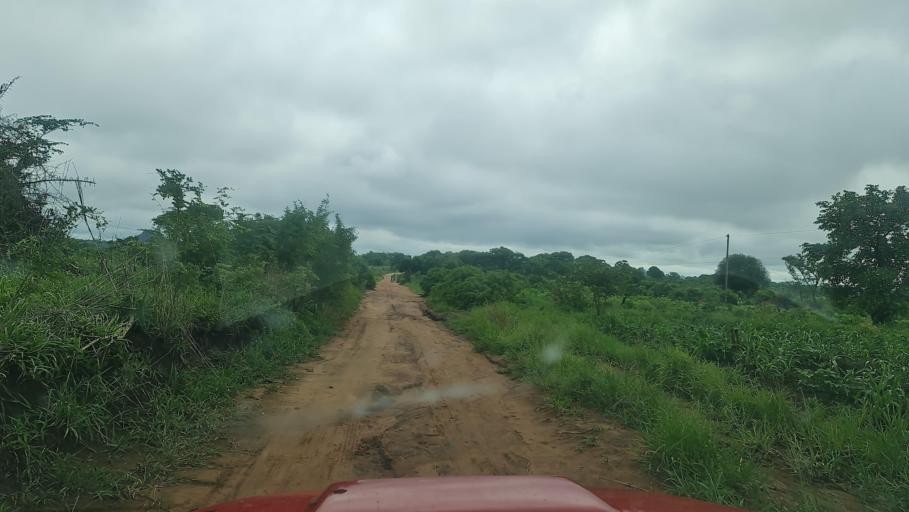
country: MW
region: Southern Region
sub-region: Nsanje District
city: Nsanje
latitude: -17.1933
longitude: 35.8491
